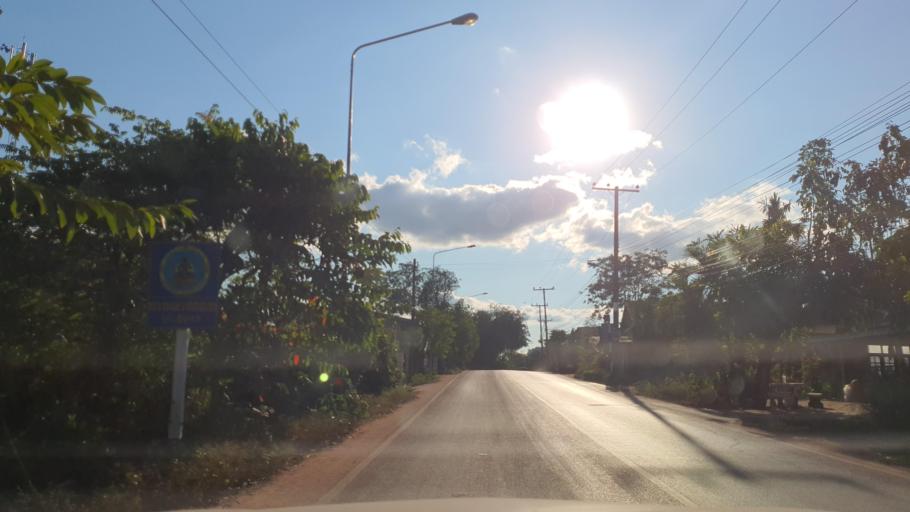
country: TH
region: Changwat Bueng Kan
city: Si Wilai
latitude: 18.1513
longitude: 103.9033
